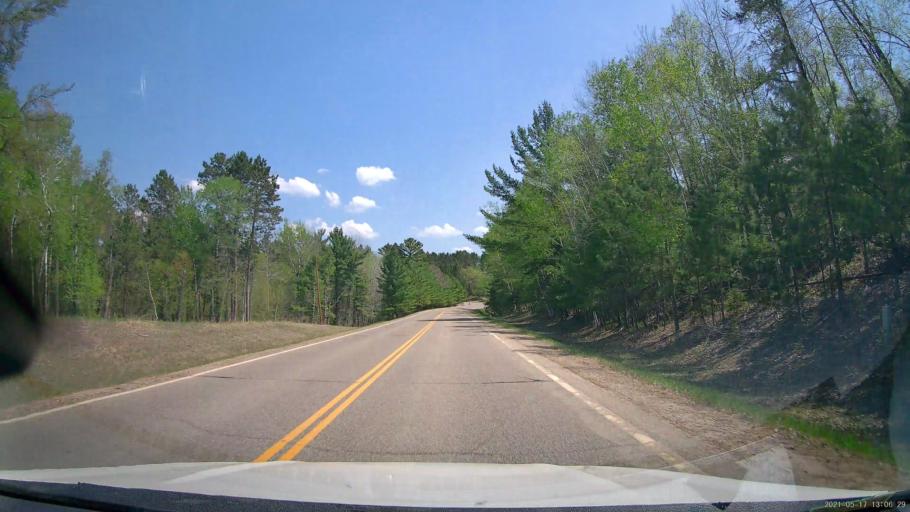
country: US
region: Minnesota
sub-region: Hubbard County
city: Park Rapids
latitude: 47.0541
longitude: -94.9256
